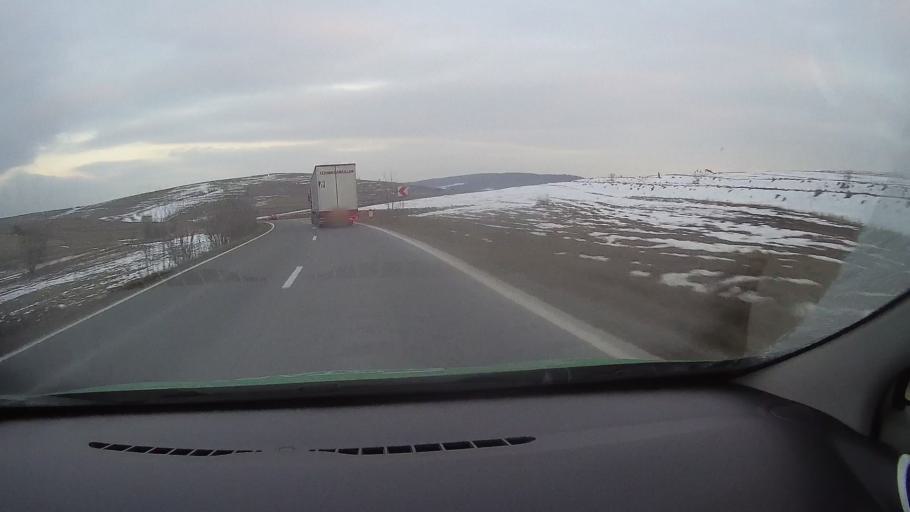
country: RO
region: Harghita
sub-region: Comuna Lupeni
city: Lupeni
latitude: 46.3510
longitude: 25.2579
